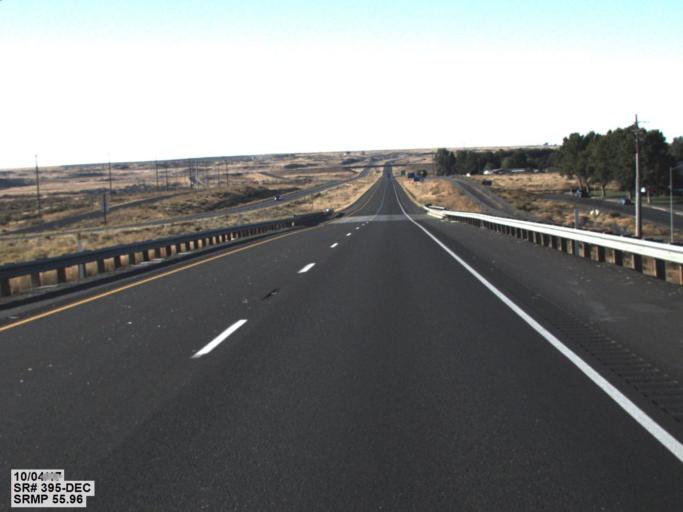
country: US
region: Washington
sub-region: Franklin County
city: Connell
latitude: 46.6639
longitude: -118.8496
